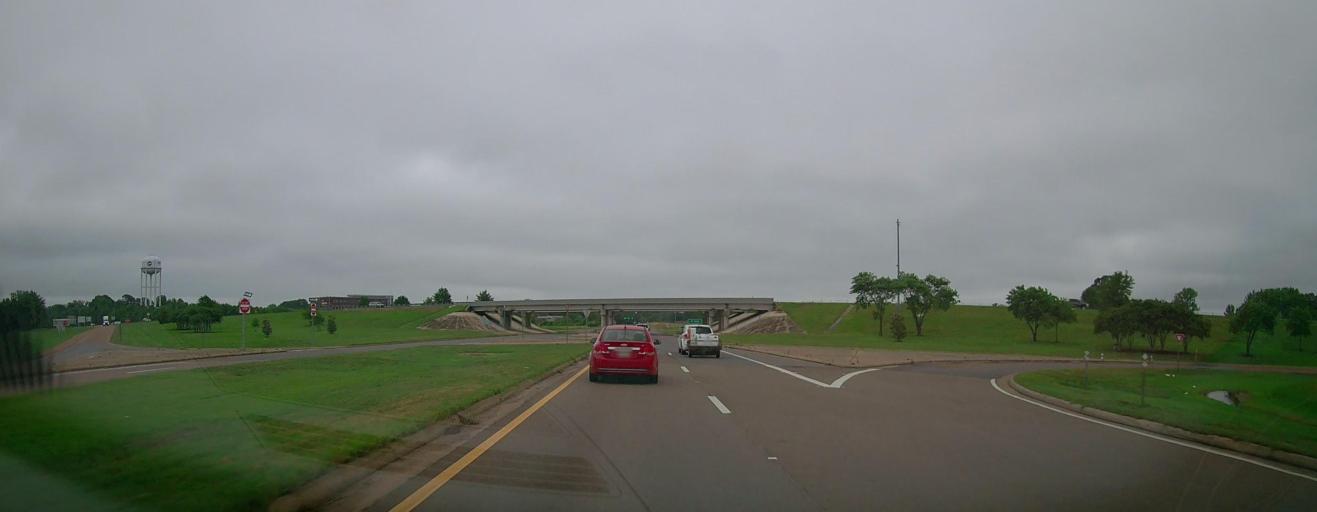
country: US
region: Mississippi
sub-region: De Soto County
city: Olive Branch
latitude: 34.9287
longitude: -89.7951
